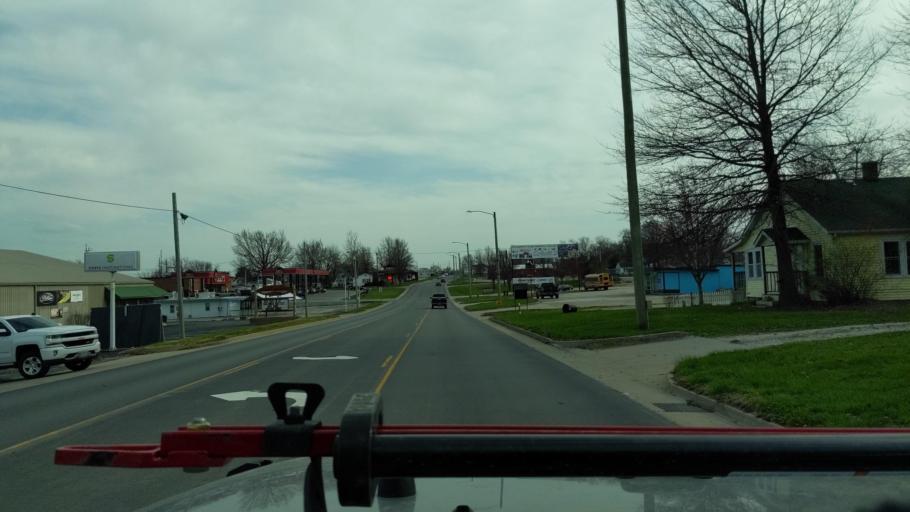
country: US
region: Missouri
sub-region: Macon County
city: Macon
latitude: 39.7307
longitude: -92.4658
